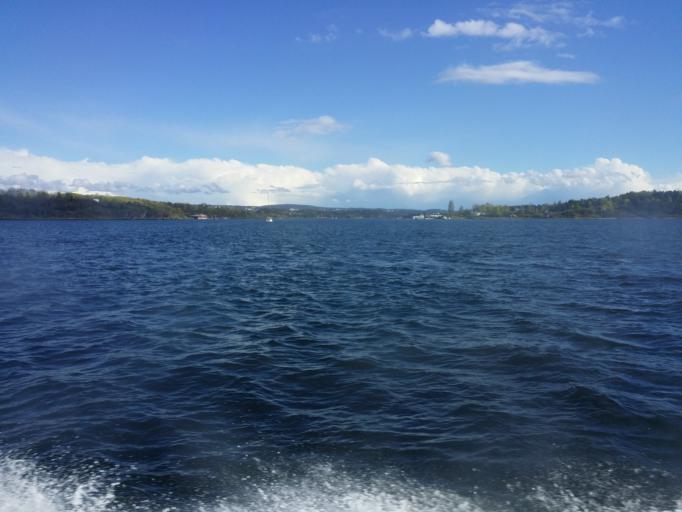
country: NO
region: Oslo
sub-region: Oslo
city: Oslo
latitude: 59.9001
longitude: 10.7136
